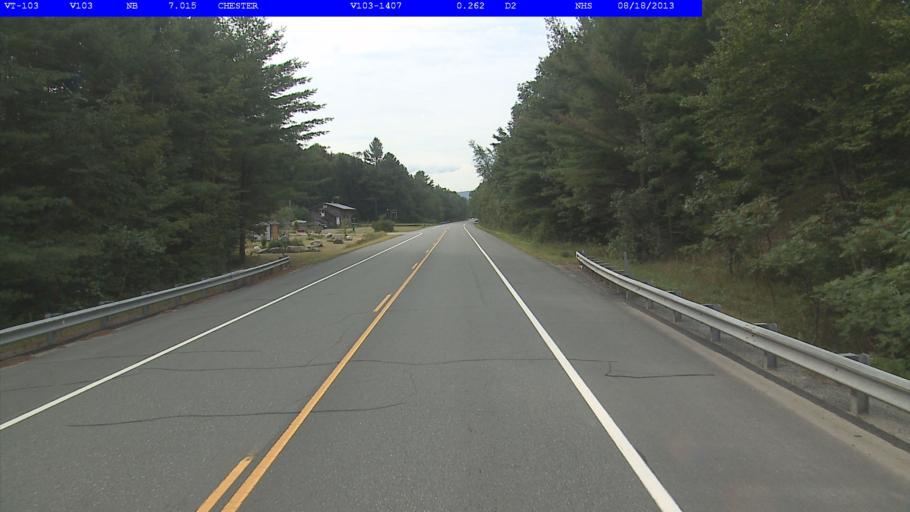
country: US
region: Vermont
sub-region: Windsor County
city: Chester
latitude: 43.2377
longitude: -72.5568
